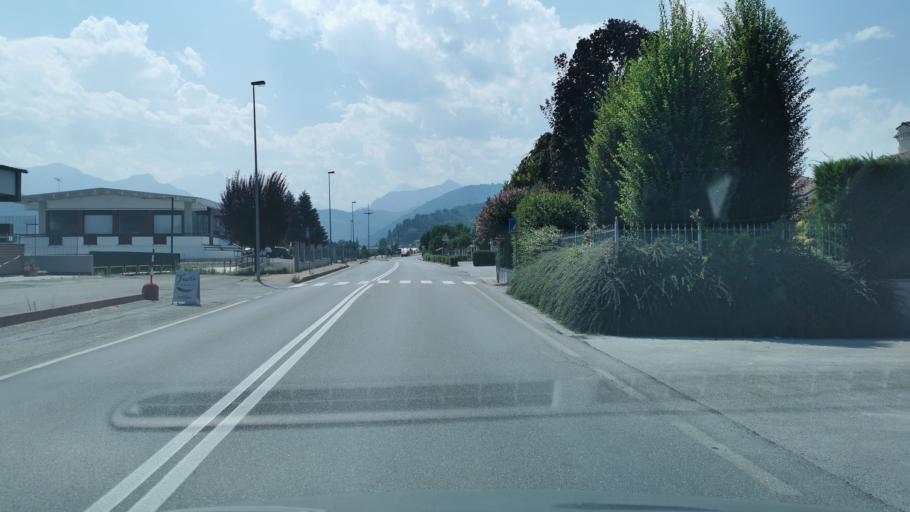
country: IT
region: Piedmont
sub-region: Provincia di Cuneo
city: Borgo San Dalmazzo
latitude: 44.3334
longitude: 7.4997
